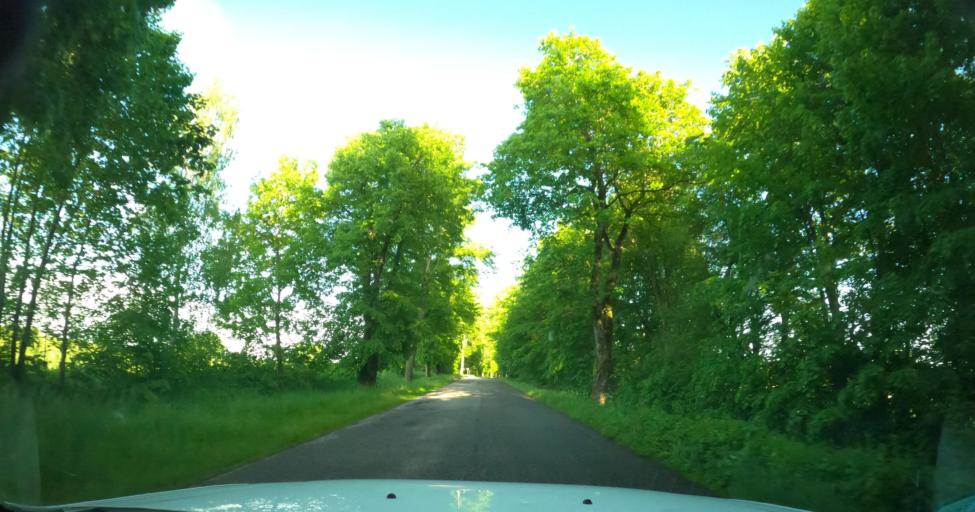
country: PL
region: Warmian-Masurian Voivodeship
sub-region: Powiat braniewski
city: Pieniezno
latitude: 54.2505
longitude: 20.0131
